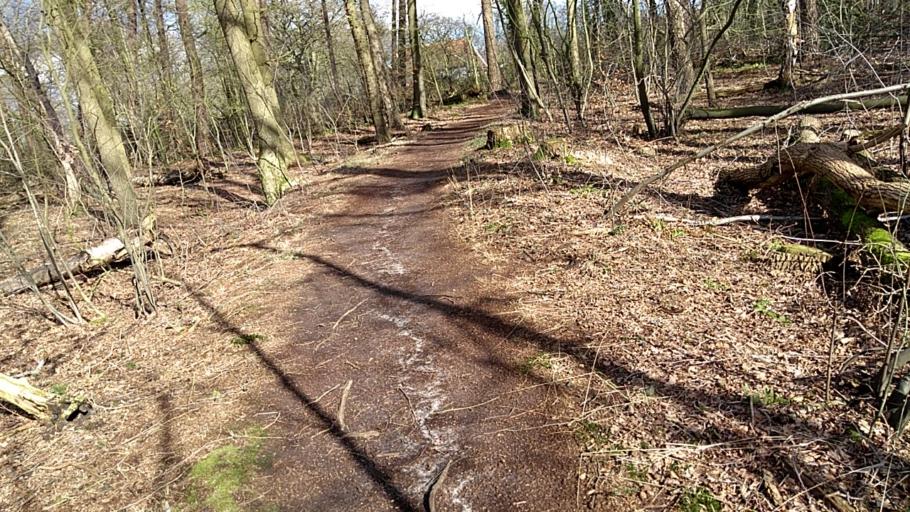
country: NL
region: Gelderland
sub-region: Gemeente Winterswijk
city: Winterswijk
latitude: 51.9963
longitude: 6.6640
